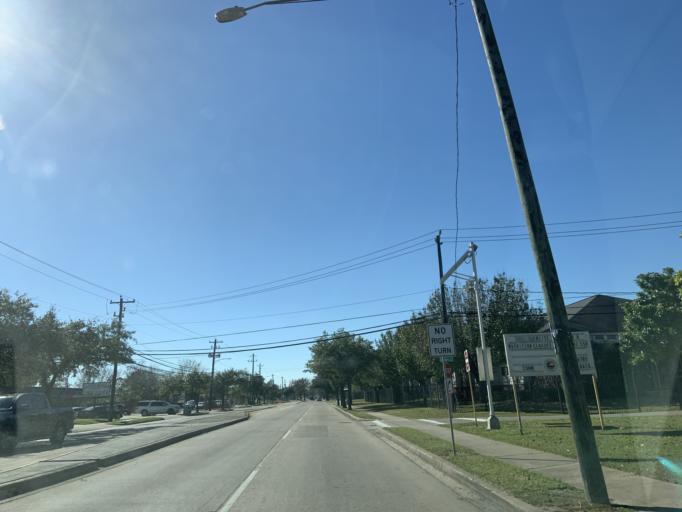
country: US
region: Texas
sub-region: Harris County
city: Bellaire
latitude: 29.6914
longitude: -95.4999
